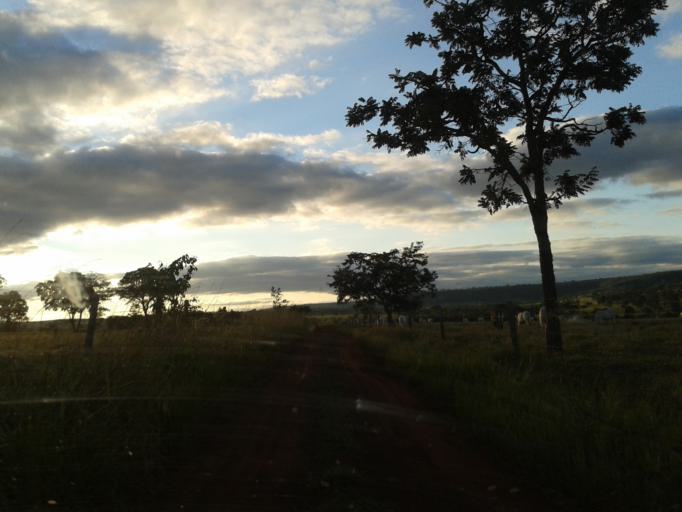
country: BR
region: Minas Gerais
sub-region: Campina Verde
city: Campina Verde
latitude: -19.5078
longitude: -49.6808
